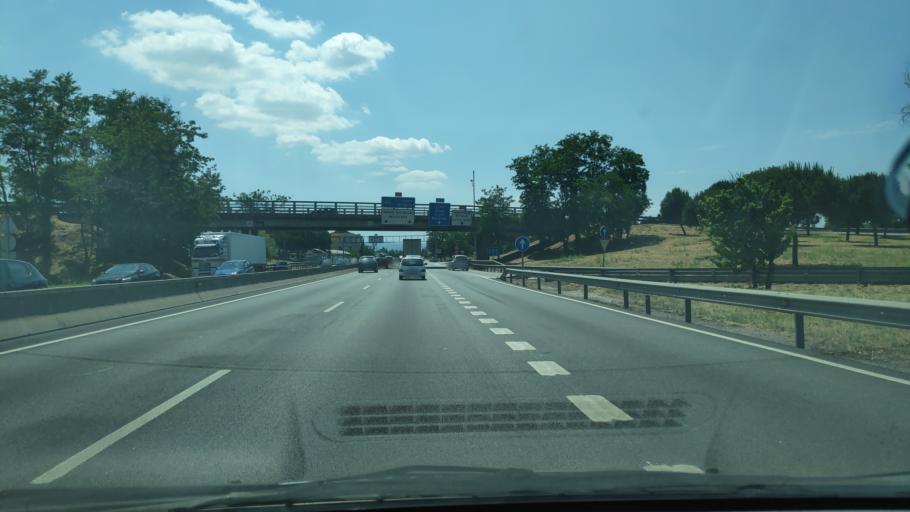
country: ES
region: Catalonia
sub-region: Provincia de Barcelona
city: Parets del Valles
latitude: 41.5702
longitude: 2.2453
